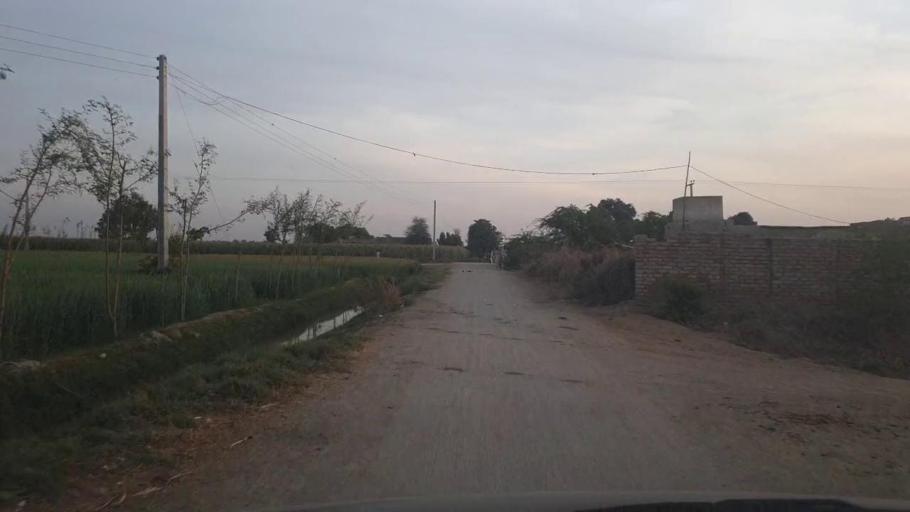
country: PK
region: Sindh
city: Kunri
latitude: 25.2217
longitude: 69.5545
